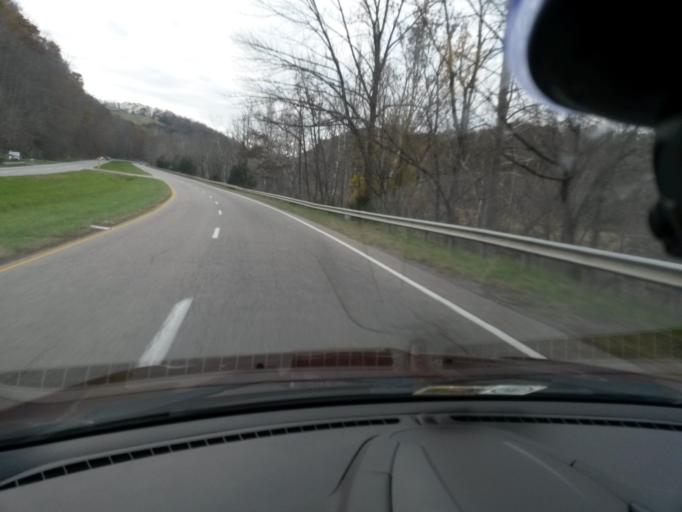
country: US
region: Virginia
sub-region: City of Buena Vista
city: Buena Vista
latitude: 37.7479
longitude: -79.3861
